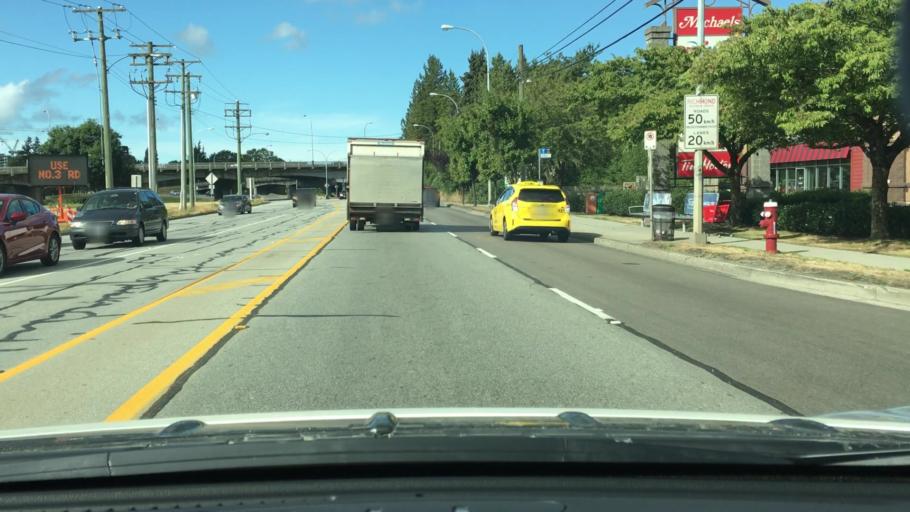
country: CA
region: British Columbia
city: Richmond
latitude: 49.1920
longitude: -123.1156
